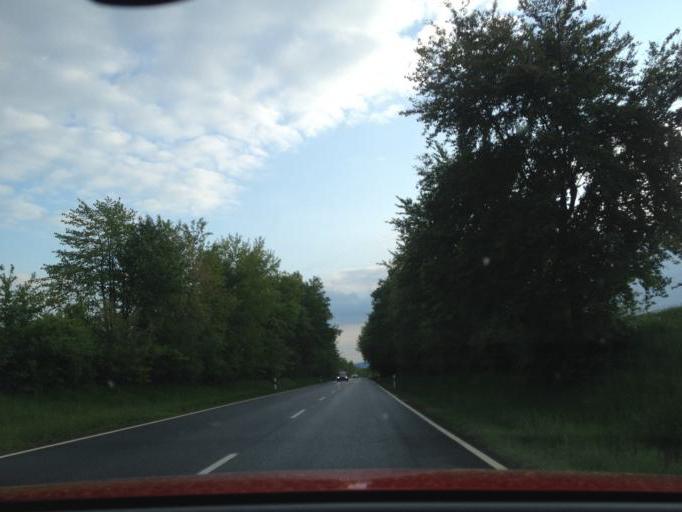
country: DE
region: Bavaria
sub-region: Upper Palatinate
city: Etzenricht
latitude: 49.6407
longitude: 12.1146
